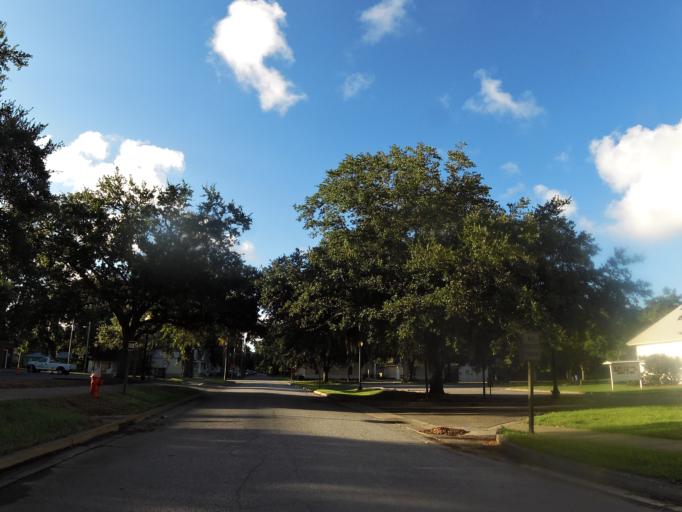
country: US
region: Georgia
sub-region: Glynn County
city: Brunswick
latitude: 31.1543
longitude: -81.4943
